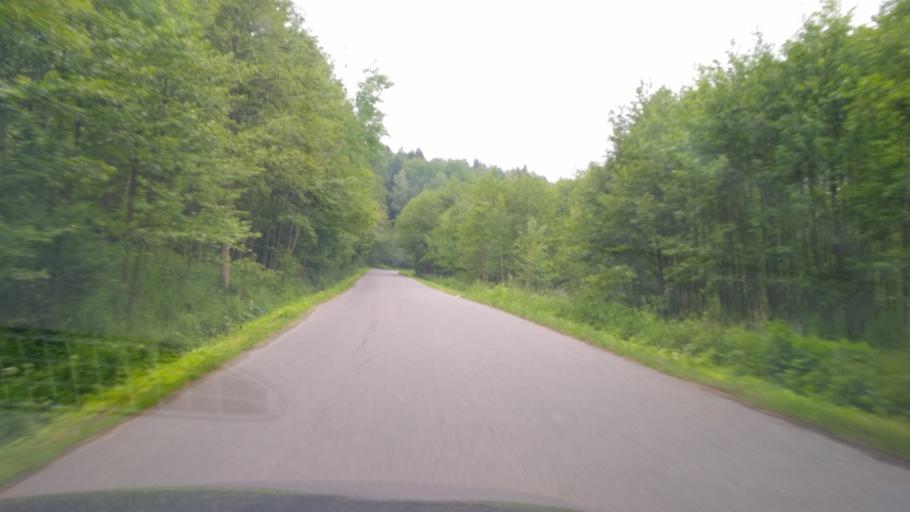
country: PL
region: Subcarpathian Voivodeship
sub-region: Powiat ropczycko-sedziszowski
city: Zagorzyce
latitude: 50.0029
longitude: 21.6842
